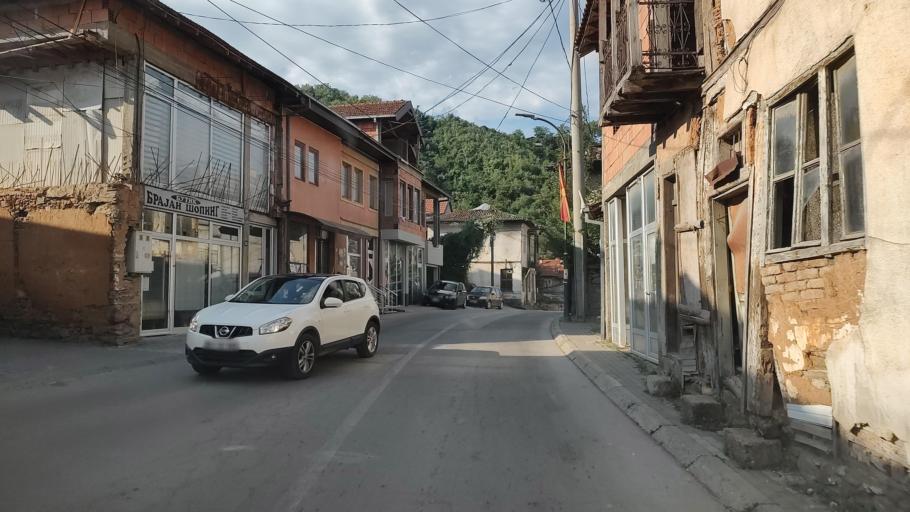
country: MK
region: Kriva Palanka
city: Kriva Palanka
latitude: 42.2009
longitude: 22.3341
